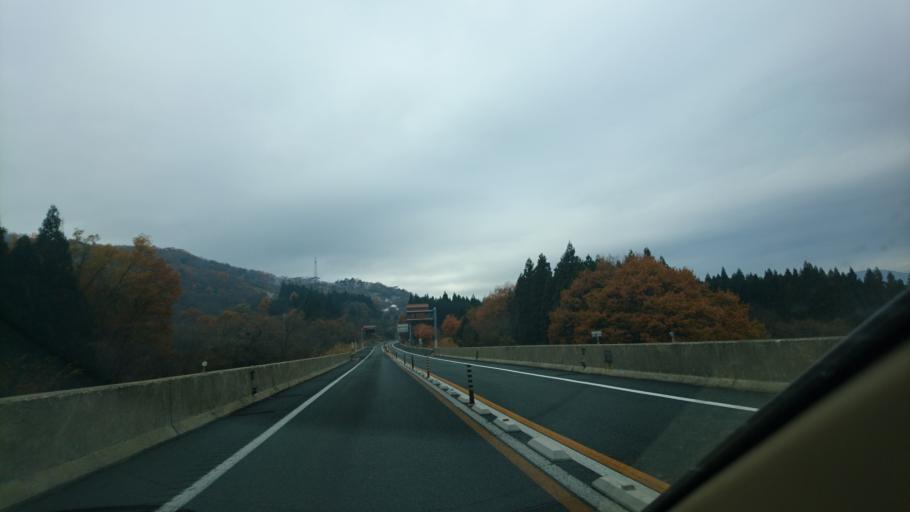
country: JP
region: Iwate
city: Kitakami
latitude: 39.2930
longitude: 140.9766
